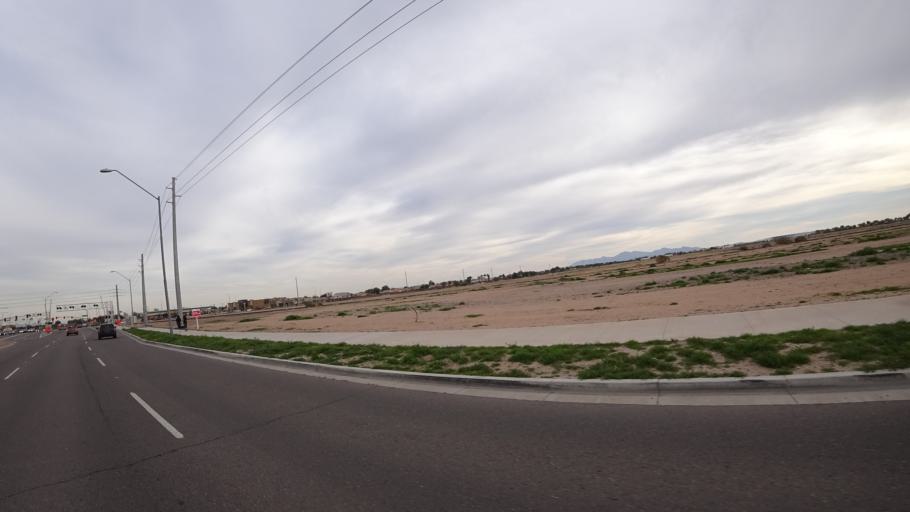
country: US
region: Arizona
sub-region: Maricopa County
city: El Mirage
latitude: 33.6090
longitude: -112.3446
